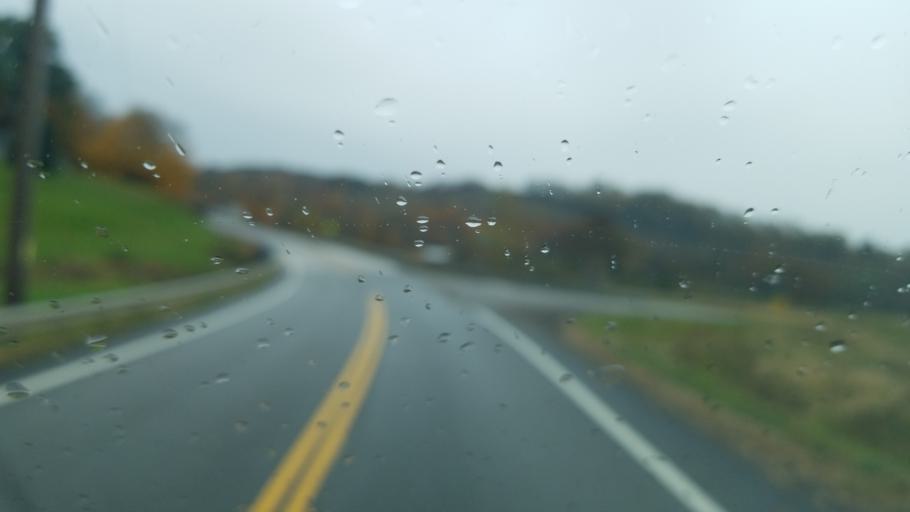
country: US
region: Ohio
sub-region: Coshocton County
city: Coshocton
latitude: 40.3607
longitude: -81.8467
